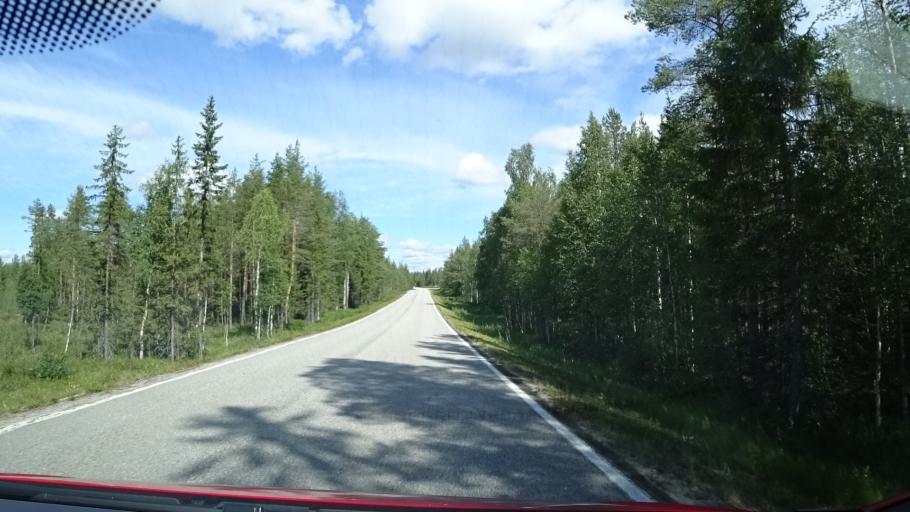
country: FI
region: Kainuu
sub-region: Kehys-Kainuu
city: Kuhmo
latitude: 64.6180
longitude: 29.6968
